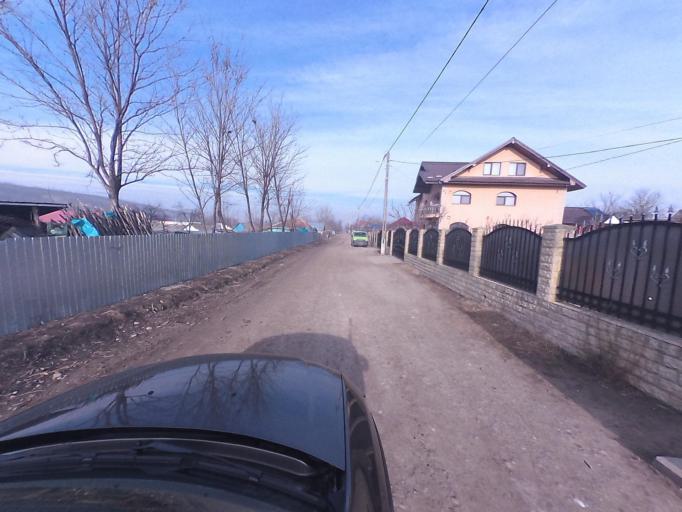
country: RO
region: Vaslui
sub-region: Comuna Solesti
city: Solesti
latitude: 46.8063
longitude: 27.7850
